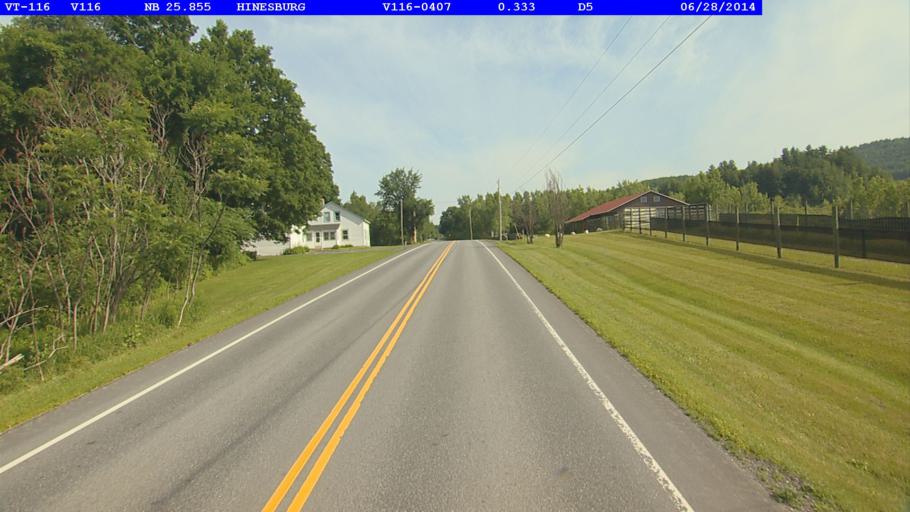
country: US
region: Vermont
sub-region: Chittenden County
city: Hinesburg
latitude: 44.2849
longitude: -73.0691
